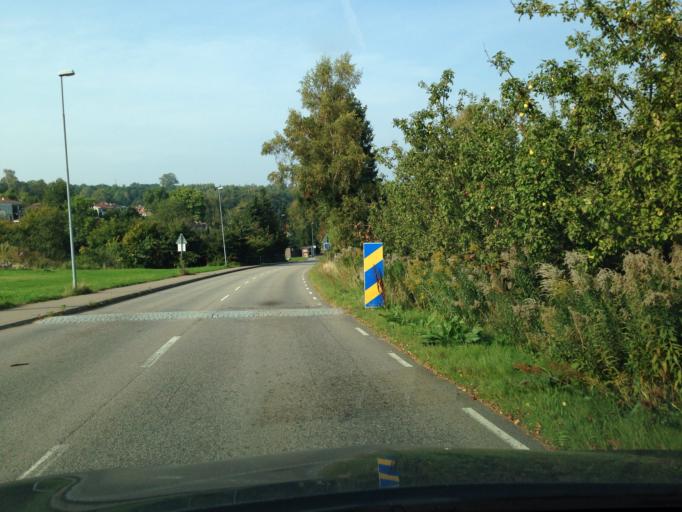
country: SE
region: Skane
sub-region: Bastads Kommun
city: Bastad
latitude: 56.4173
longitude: 12.8467
